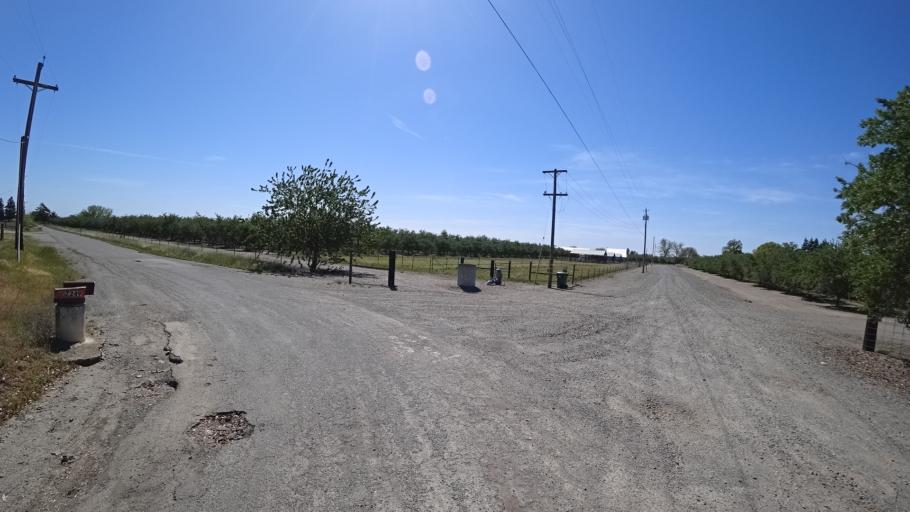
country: US
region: California
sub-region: Glenn County
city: Orland
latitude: 39.7395
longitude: -122.1138
